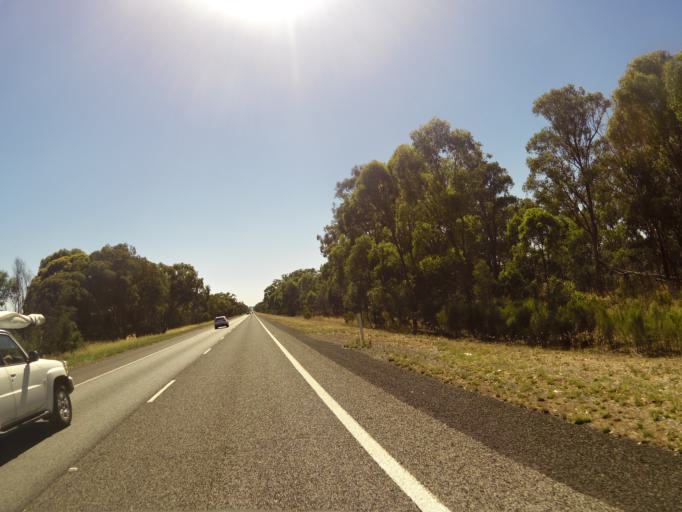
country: AU
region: Victoria
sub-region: Greater Shepparton
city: Shepparton
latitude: -36.8606
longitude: 145.3079
